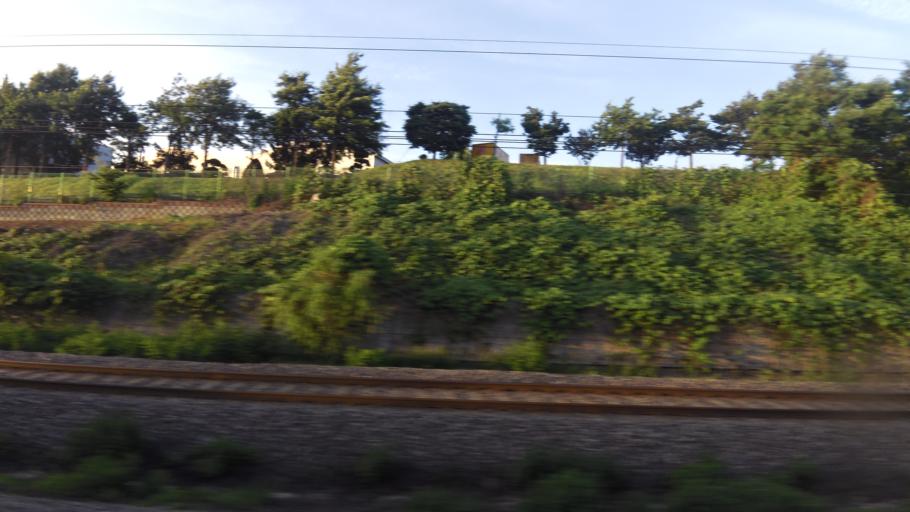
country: KR
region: Gyeonggi-do
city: Osan
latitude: 37.0424
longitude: 127.0607
